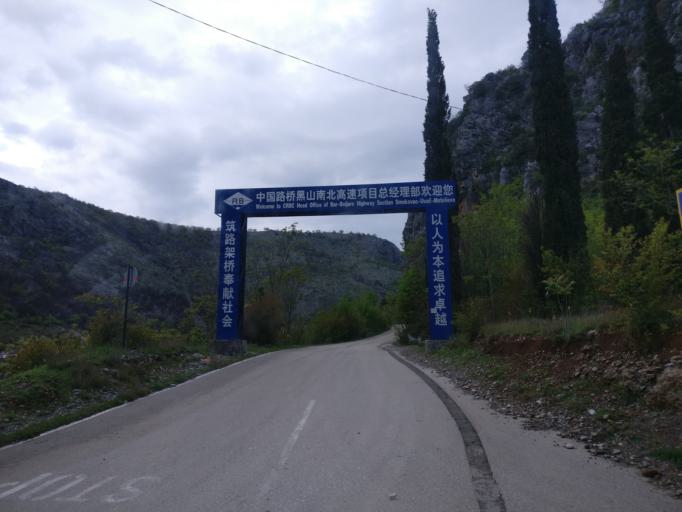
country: ME
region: Podgorica
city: Podgorica
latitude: 42.5164
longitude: 19.3455
